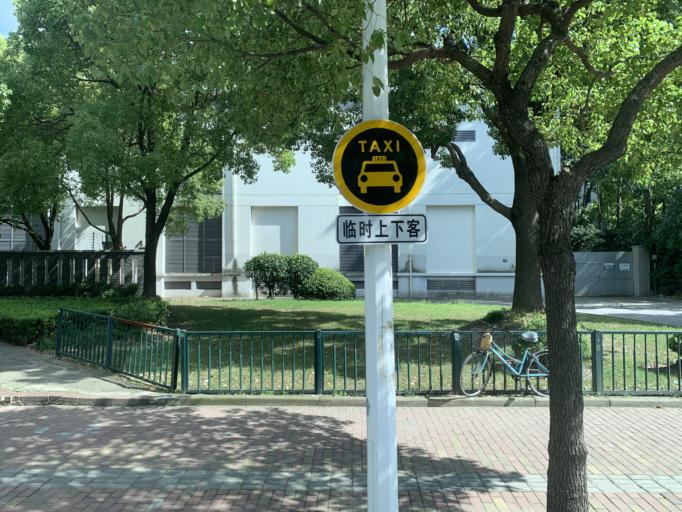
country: CN
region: Shanghai Shi
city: Pudong
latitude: 31.2393
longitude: 121.5314
